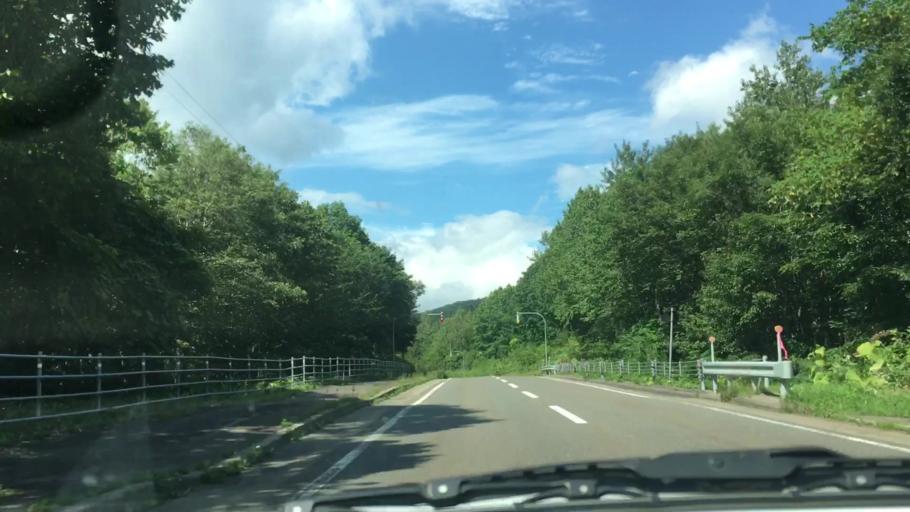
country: JP
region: Hokkaido
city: Otofuke
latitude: 43.3376
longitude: 143.2869
